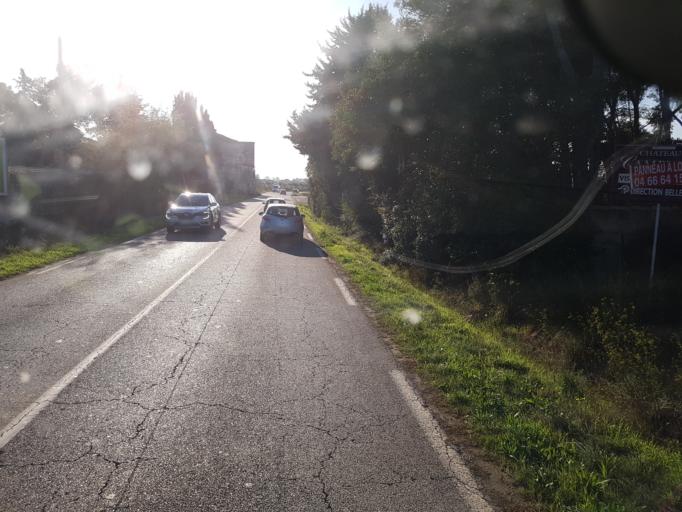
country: FR
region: Languedoc-Roussillon
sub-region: Departement du Gard
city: Redessan
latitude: 43.8267
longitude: 4.5027
